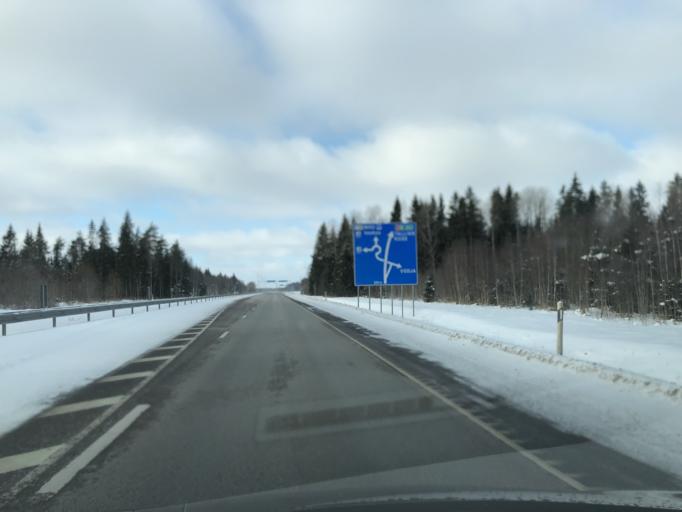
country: EE
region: Jaervamaa
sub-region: Paide linn
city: Paide
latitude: 58.8962
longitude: 25.6573
